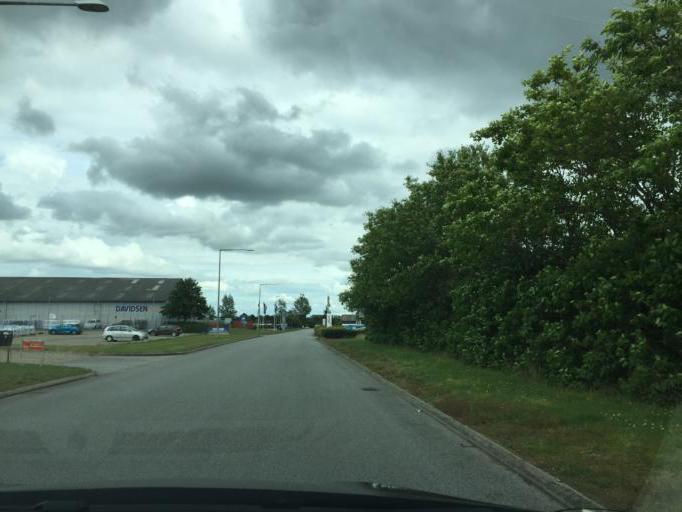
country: DK
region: South Denmark
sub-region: Haderslev Kommune
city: Vojens
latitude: 55.2409
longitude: 9.2720
